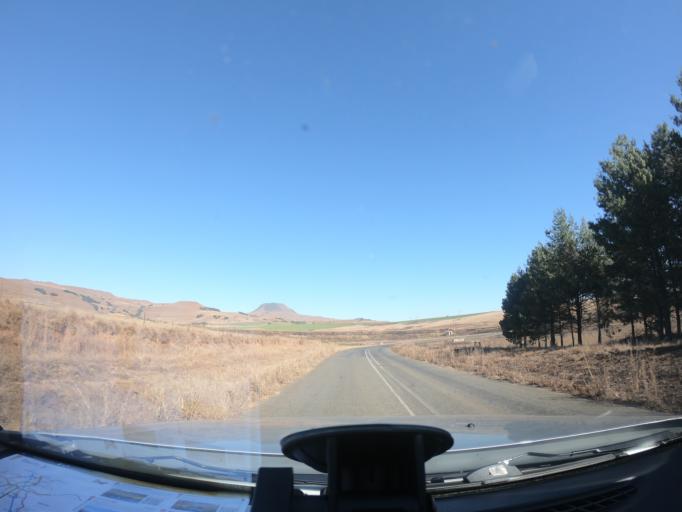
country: ZA
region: KwaZulu-Natal
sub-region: uMgungundlovu District Municipality
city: Mooirivier
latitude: -29.3338
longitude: 29.8166
